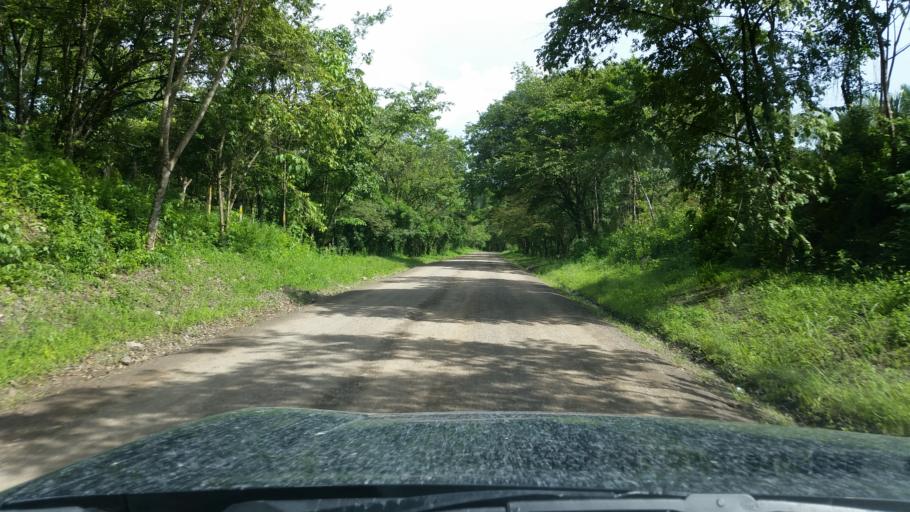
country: NI
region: Atlantico Norte (RAAN)
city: Siuna
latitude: 13.6667
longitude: -84.7923
